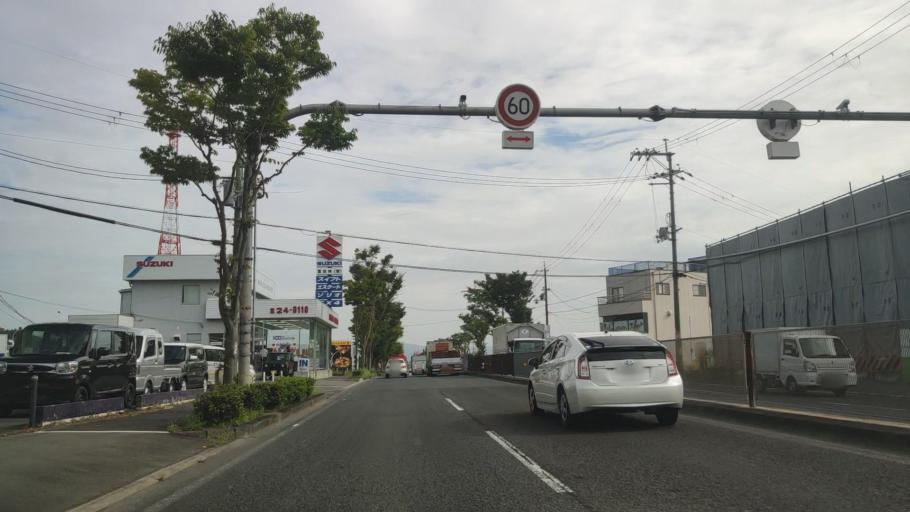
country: JP
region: Osaka
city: Tondabayashicho
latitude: 34.5105
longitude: 135.6021
